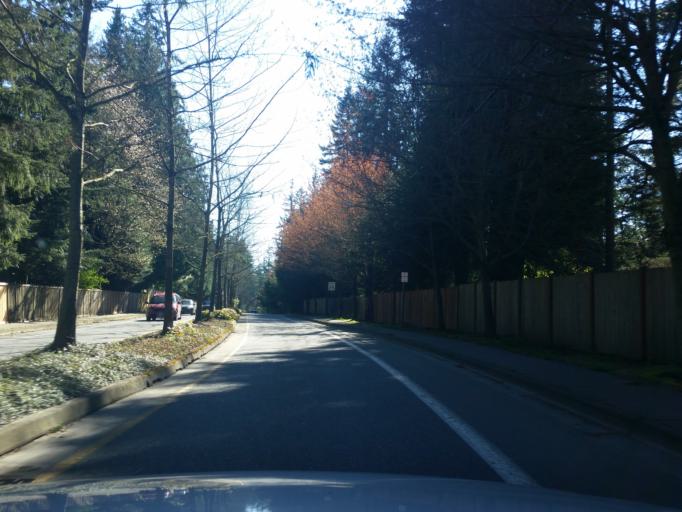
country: US
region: Washington
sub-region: Snohomish County
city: Mill Creek
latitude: 47.8548
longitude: -122.1972
